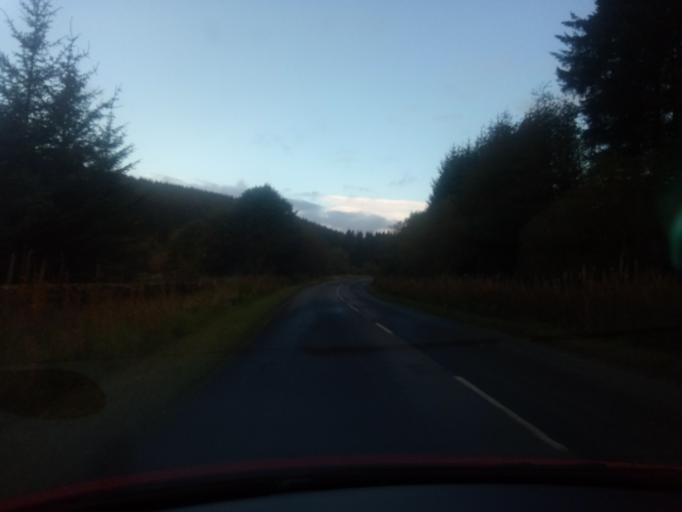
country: GB
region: Scotland
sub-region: The Scottish Borders
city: Hawick
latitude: 55.3521
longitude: -2.6466
